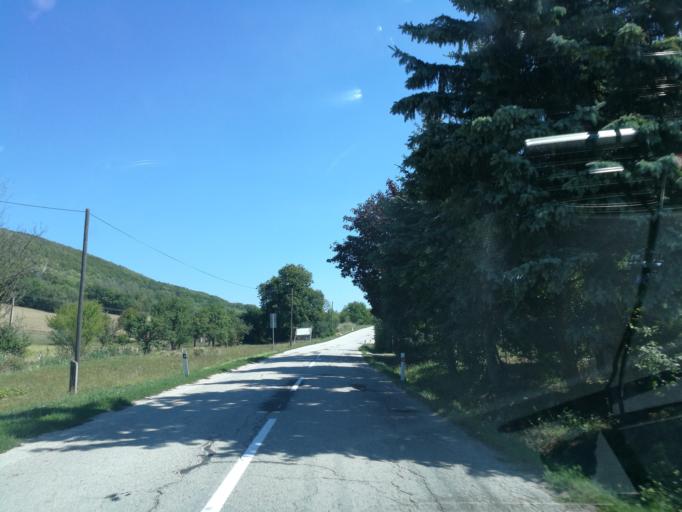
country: SK
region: Nitriansky
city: Brezova pod Bradlom
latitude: 48.6729
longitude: 17.5822
